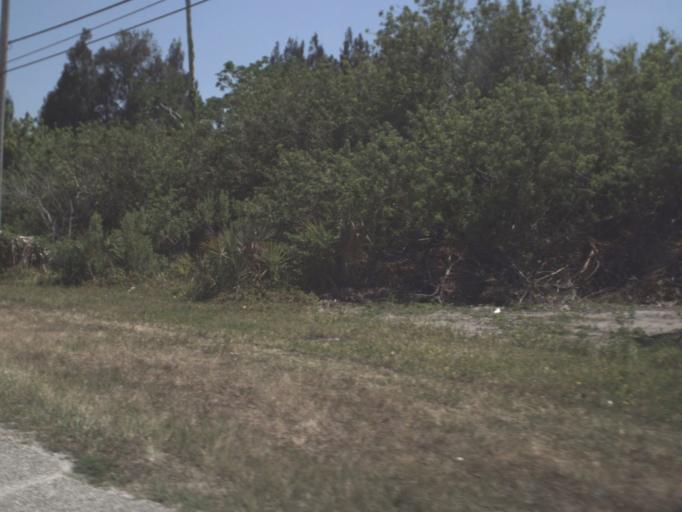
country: US
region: Florida
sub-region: Brevard County
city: Micco
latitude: 27.9170
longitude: -80.5192
